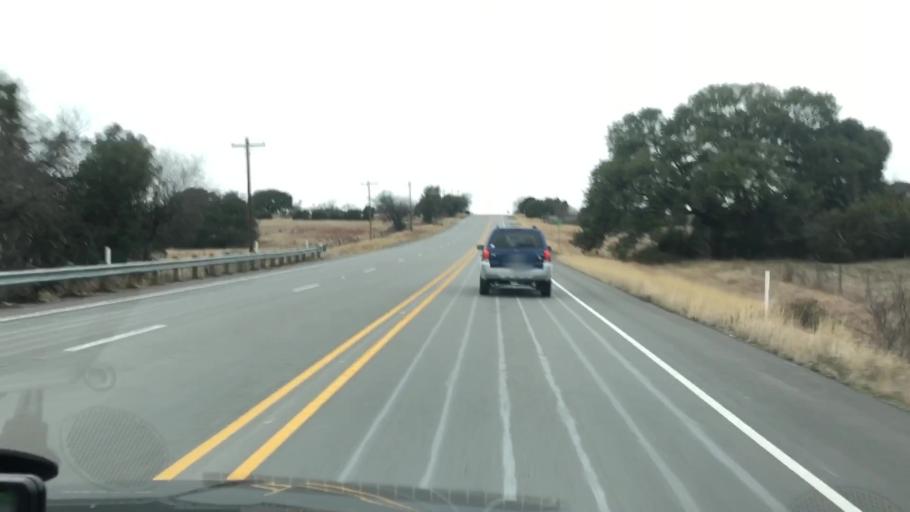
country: US
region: Texas
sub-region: Hamilton County
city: Hico
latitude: 32.0164
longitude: -98.0671
